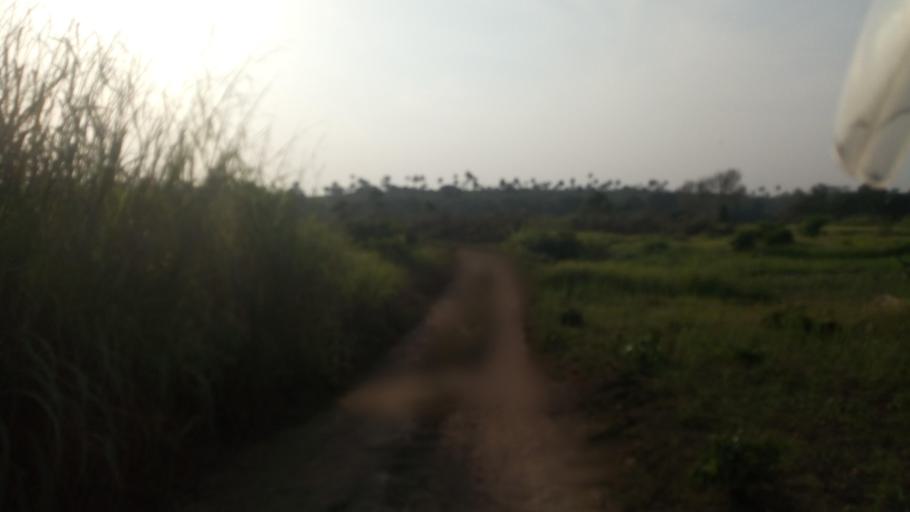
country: SL
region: Southern Province
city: Mogbwemo
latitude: 7.6016
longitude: -12.1792
